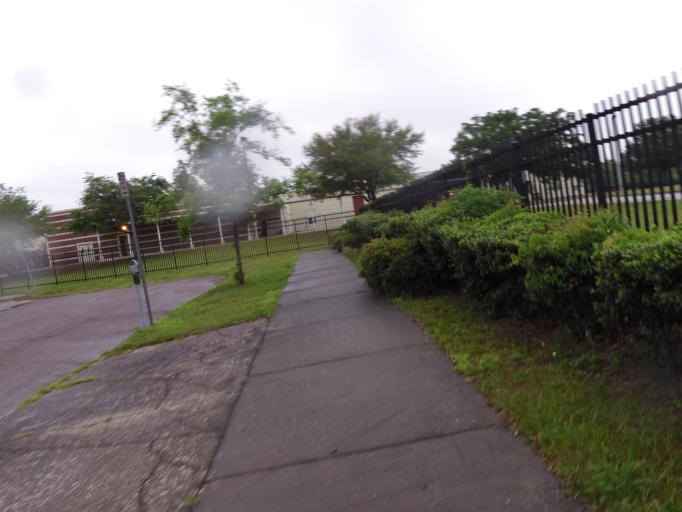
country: US
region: Florida
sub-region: Duval County
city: Jacksonville
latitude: 30.3320
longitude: -81.6658
